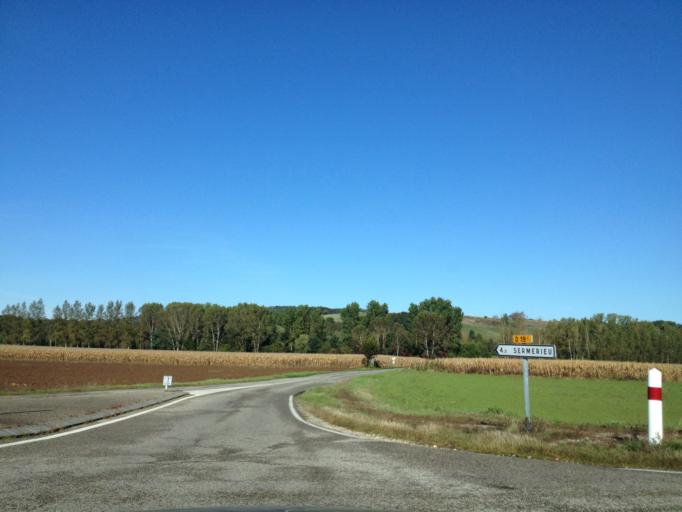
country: FR
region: Rhone-Alpes
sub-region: Departement de l'Isere
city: Morestel
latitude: 45.6598
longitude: 5.4597
